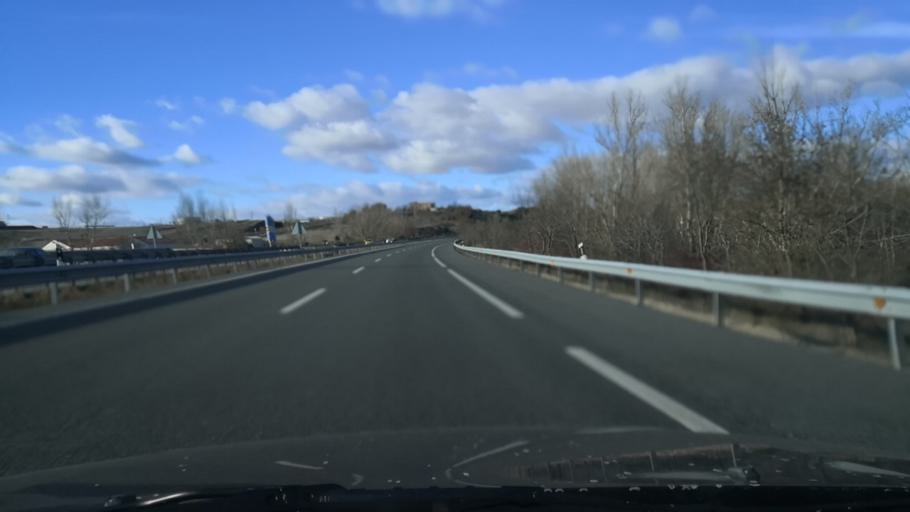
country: ES
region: Castille and Leon
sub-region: Provincia de Avila
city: Sanchidrian
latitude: 40.8654
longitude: -4.5640
